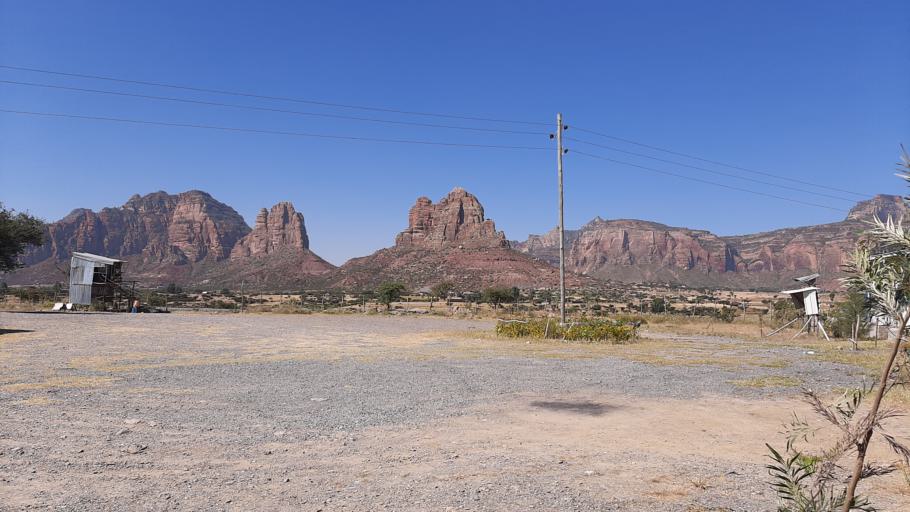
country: ET
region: Tigray
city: Adigrat
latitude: 13.9083
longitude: 39.4045
